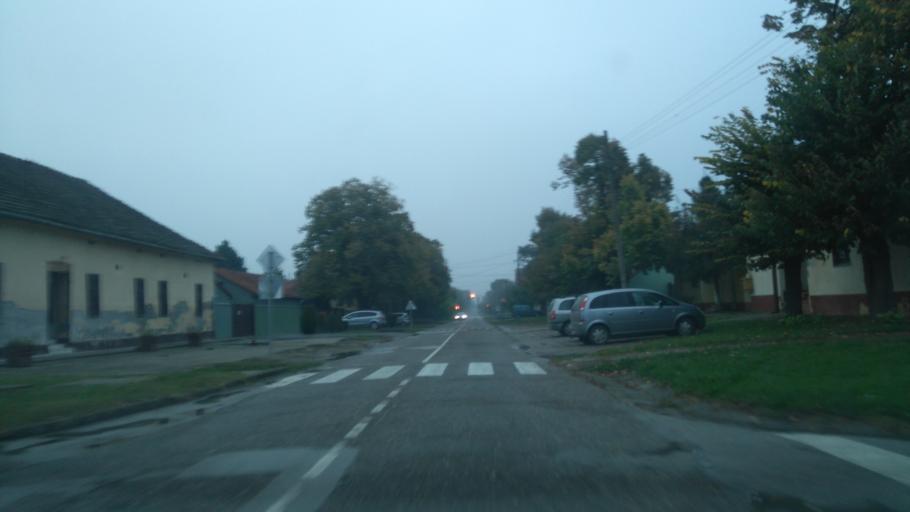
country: RS
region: Autonomna Pokrajina Vojvodina
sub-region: Juznobacki Okrug
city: Becej
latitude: 45.6119
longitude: 20.0362
